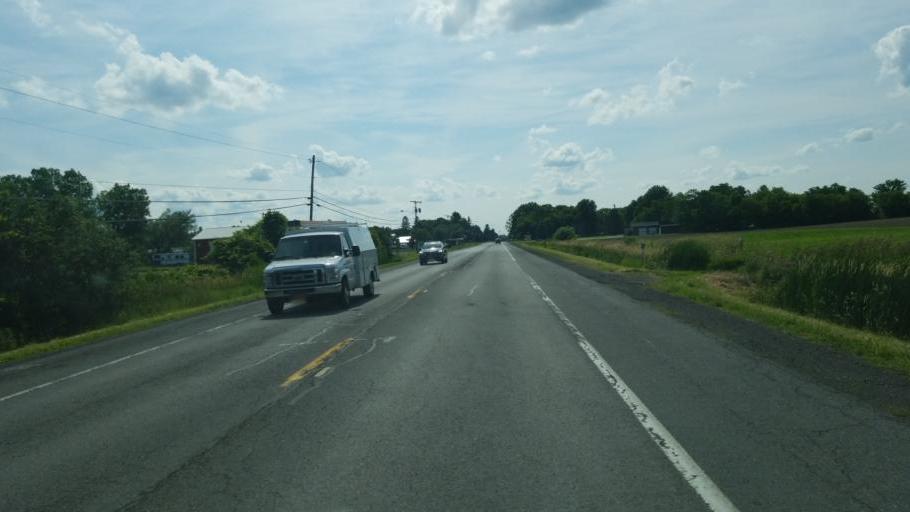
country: US
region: New York
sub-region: Ontario County
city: Canandaigua
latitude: 42.8623
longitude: -77.1913
